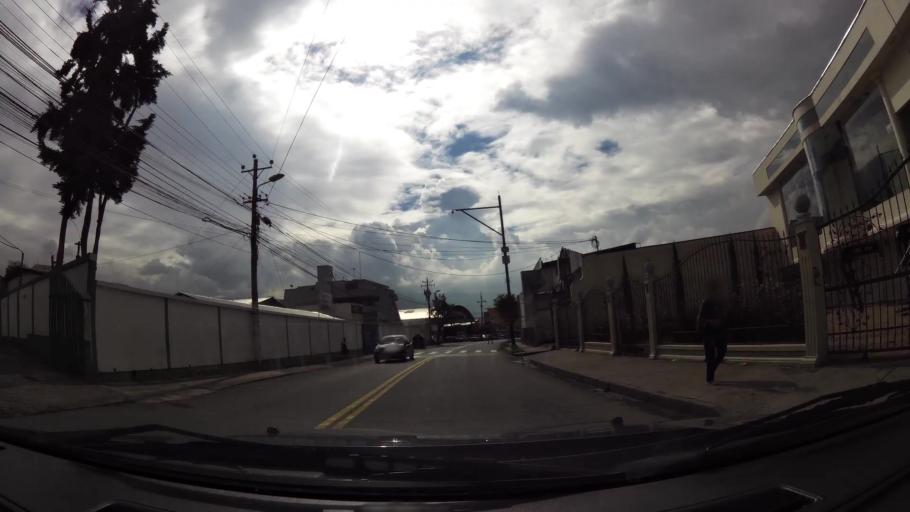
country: EC
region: Pichincha
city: Sangolqui
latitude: -0.3067
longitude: -78.4546
